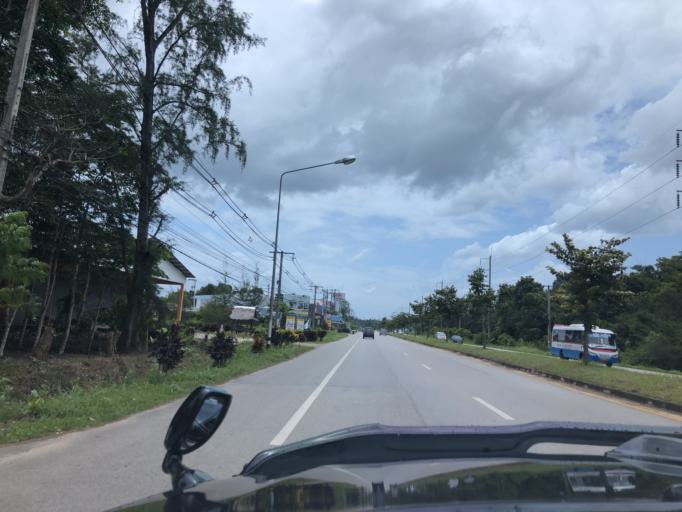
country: TH
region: Krabi
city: Khlong Thom
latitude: 7.9725
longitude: 99.1400
